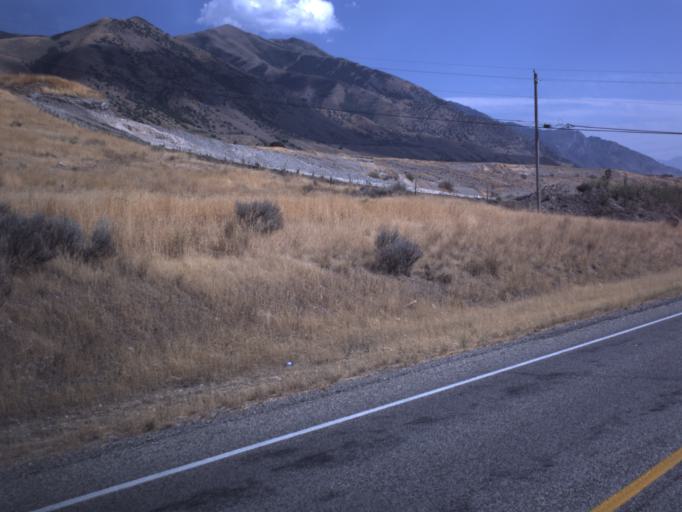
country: US
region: Utah
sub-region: Box Elder County
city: Elwood
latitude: 41.7354
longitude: -112.0987
